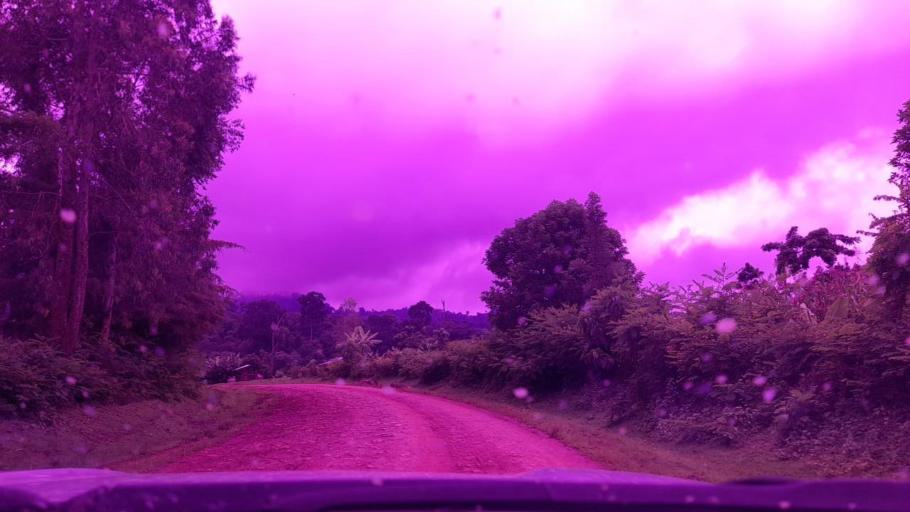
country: ET
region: Southern Nations, Nationalities, and People's Region
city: Bonga
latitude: 7.5592
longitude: 35.8411
